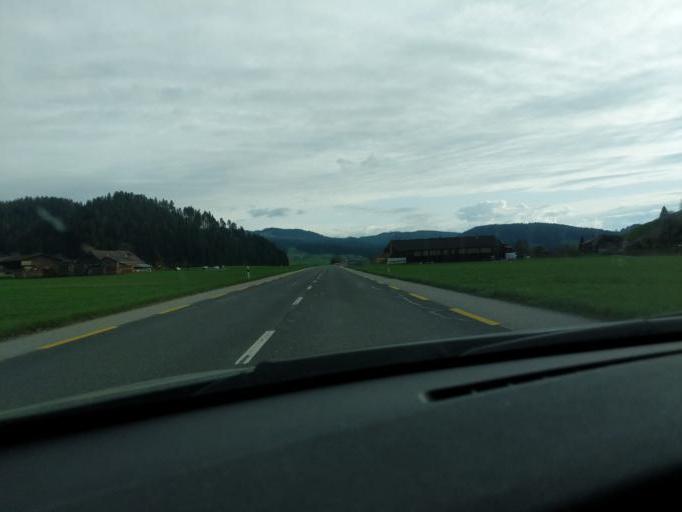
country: CH
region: Bern
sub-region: Emmental District
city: Signau
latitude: 46.9098
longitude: 7.7163
